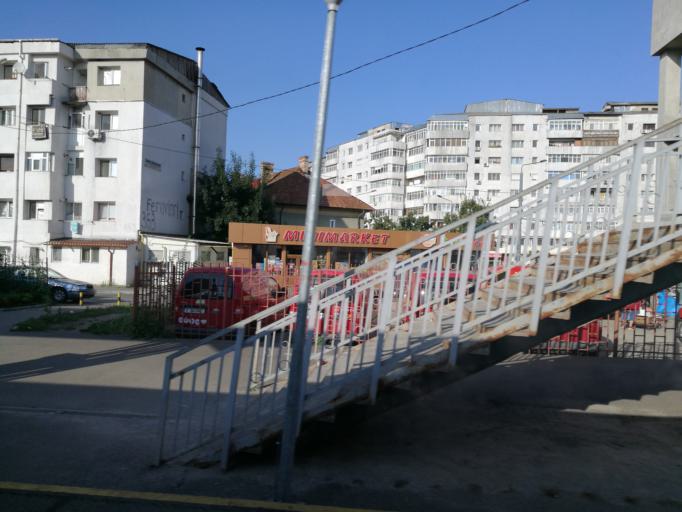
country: RO
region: Vaslui
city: Vaslui
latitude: 46.6271
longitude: 27.7267
